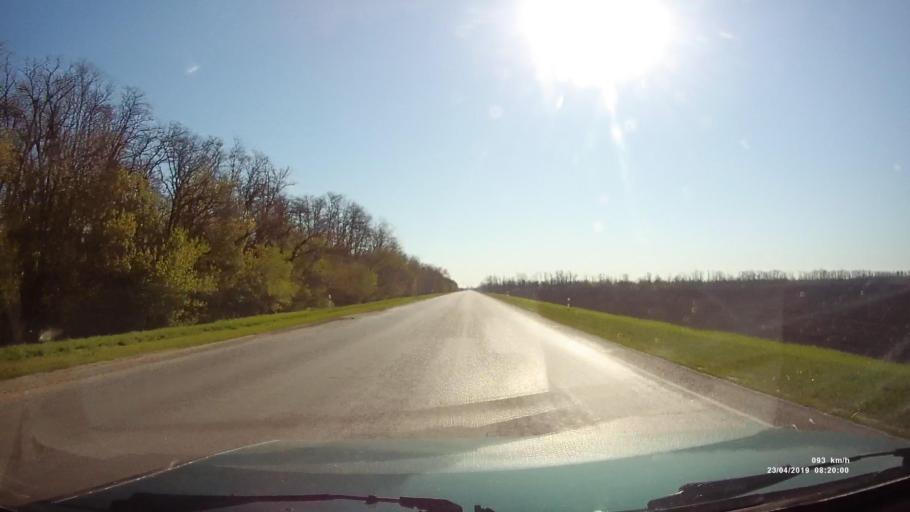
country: RU
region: Rostov
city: Tselina
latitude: 46.5373
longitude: 40.8612
